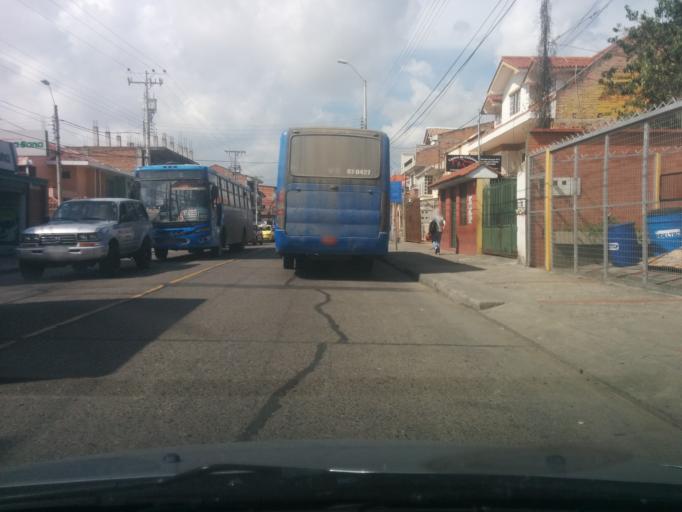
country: EC
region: Azuay
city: Cuenca
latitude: -2.8991
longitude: -78.9907
